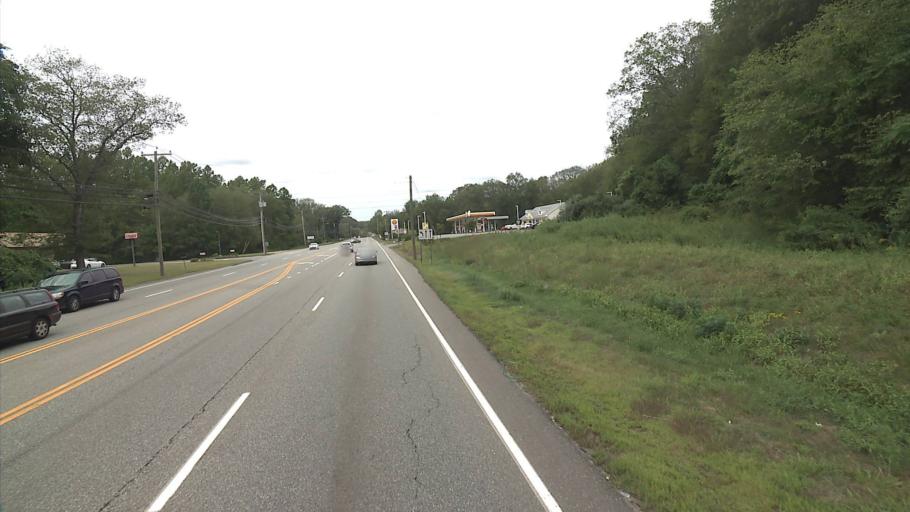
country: US
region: Connecticut
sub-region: New London County
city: Central Waterford
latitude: 41.3862
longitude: -72.1585
